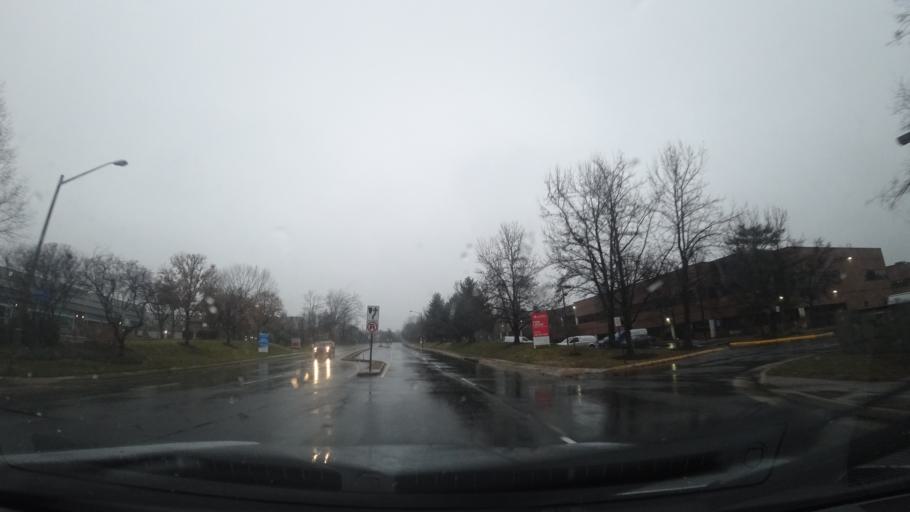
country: US
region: Virginia
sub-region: Fairfax County
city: Herndon
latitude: 38.9601
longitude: -77.3768
